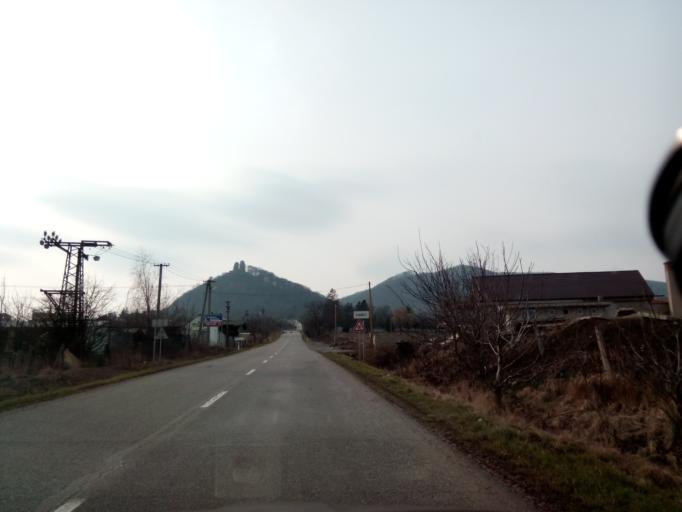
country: SK
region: Kosicky
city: Secovce
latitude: 48.6366
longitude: 21.4870
